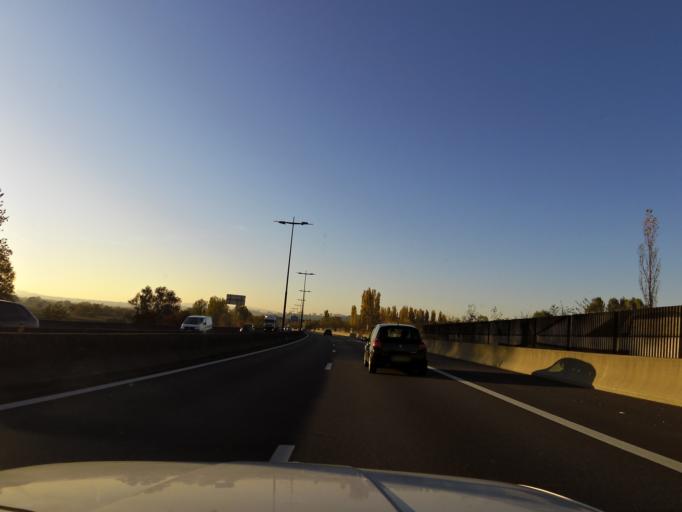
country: FR
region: Rhone-Alpes
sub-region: Departement du Rhone
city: Decines-Charpieu
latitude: 45.7933
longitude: 4.9528
